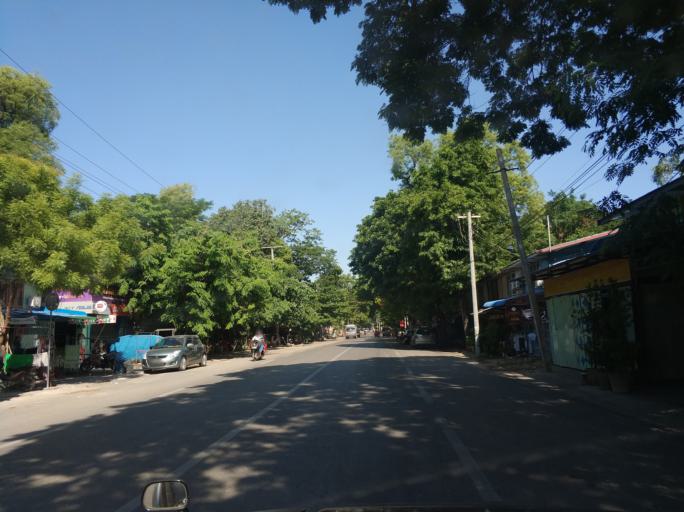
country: MM
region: Mandalay
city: Mandalay
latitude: 21.9712
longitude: 96.0600
